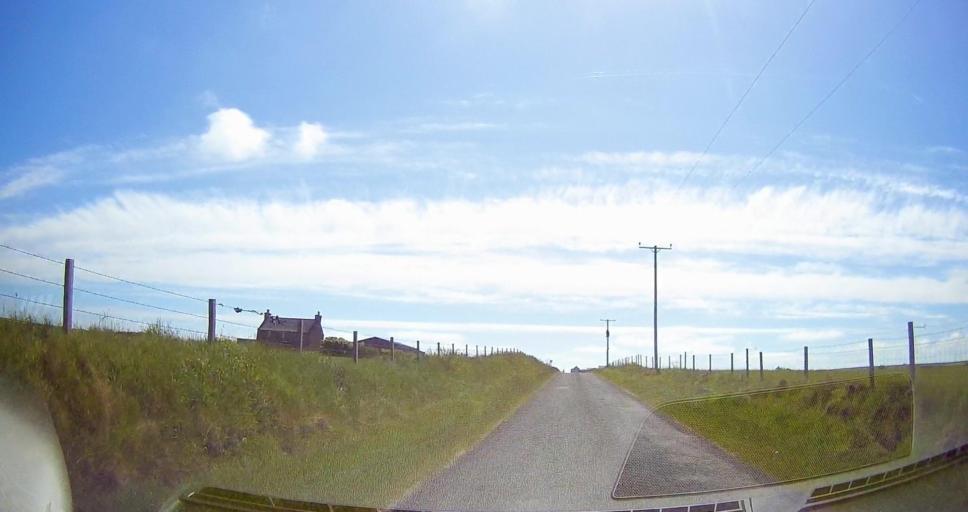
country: GB
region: Scotland
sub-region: Orkney Islands
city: Kirkwall
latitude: 58.8339
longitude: -2.9172
